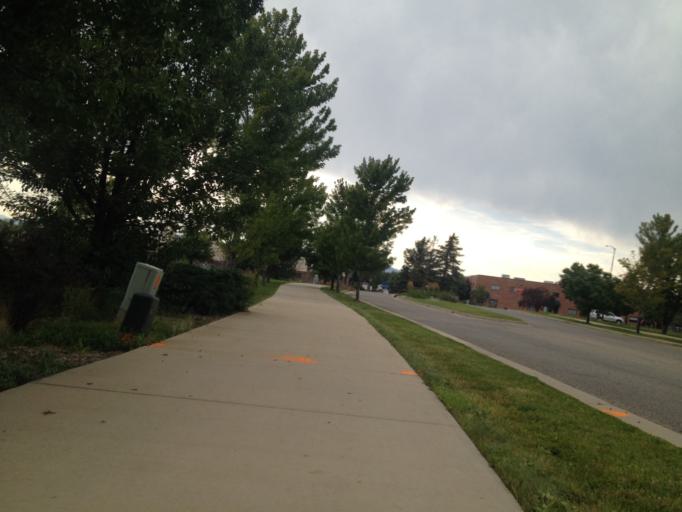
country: US
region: Colorado
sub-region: Boulder County
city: Lafayette
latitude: 39.9801
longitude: -105.0707
